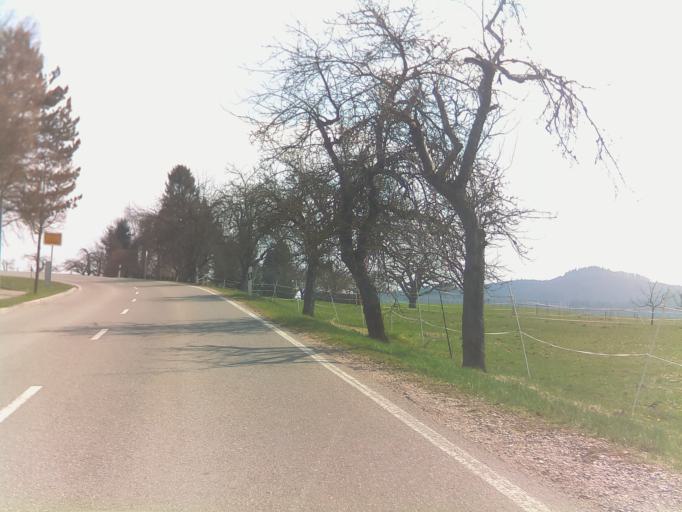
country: DE
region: Baden-Wuerttemberg
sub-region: Tuebingen Region
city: Bad Urach
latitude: 48.4559
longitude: 9.3916
